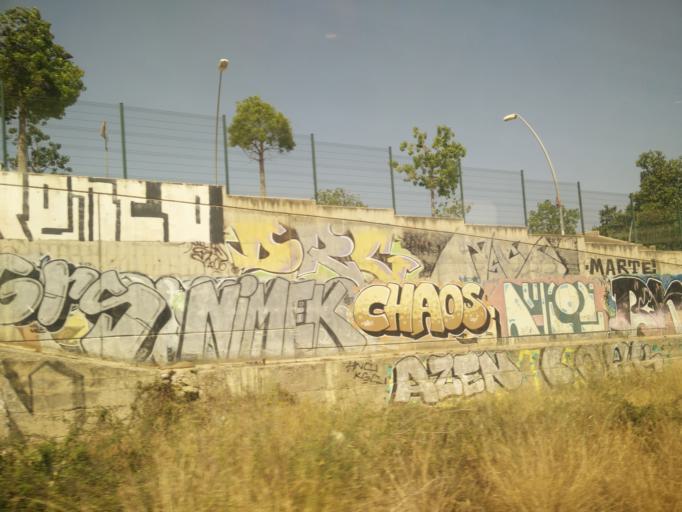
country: ES
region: Catalonia
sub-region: Provincia de Barcelona
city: Sant Adria de Besos
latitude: 41.4261
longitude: 2.2107
